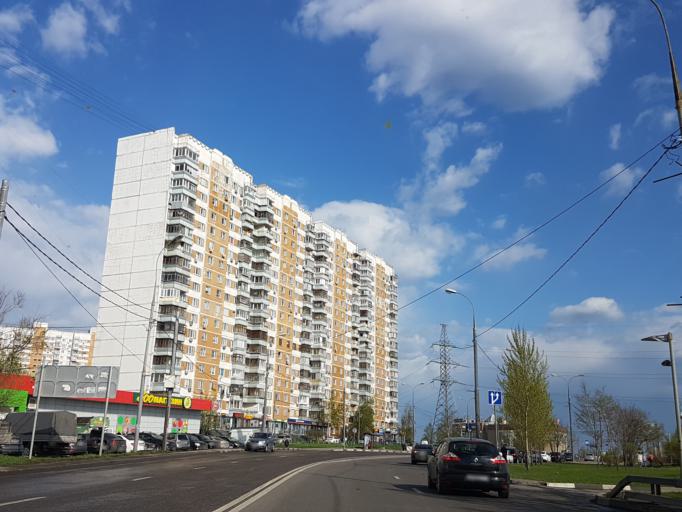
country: RU
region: Moskovskaya
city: Pavshino
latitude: 55.8377
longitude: 37.3799
